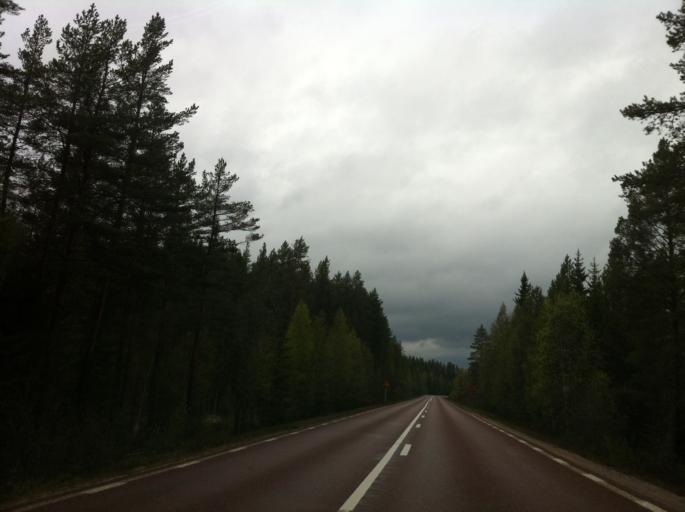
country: SE
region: Jaemtland
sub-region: Harjedalens Kommun
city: Sveg
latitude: 61.8880
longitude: 14.6252
